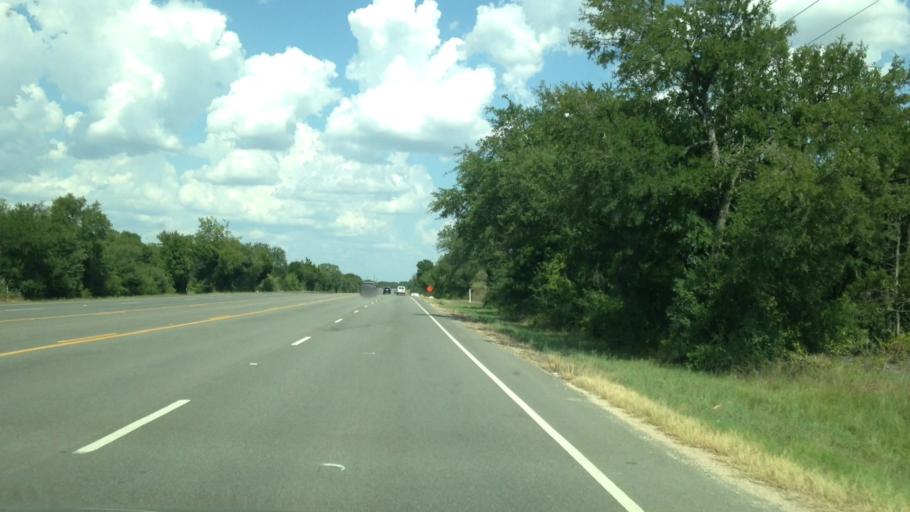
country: US
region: Texas
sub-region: Williamson County
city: Georgetown
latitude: 30.6317
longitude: -97.7397
